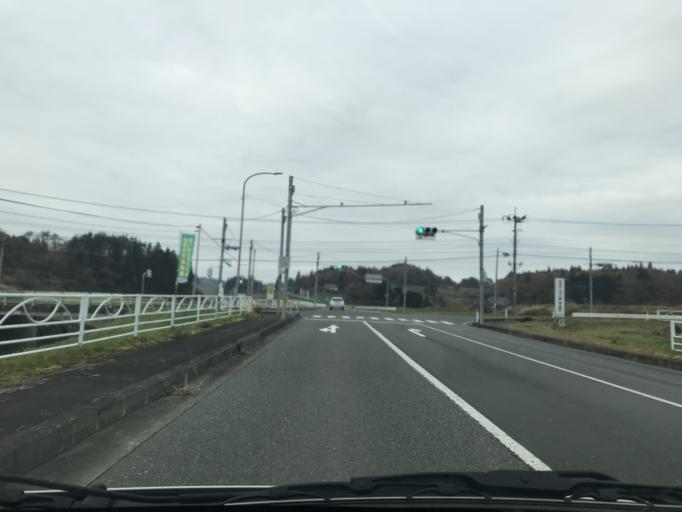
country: JP
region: Iwate
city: Mizusawa
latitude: 39.1905
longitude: 141.2229
